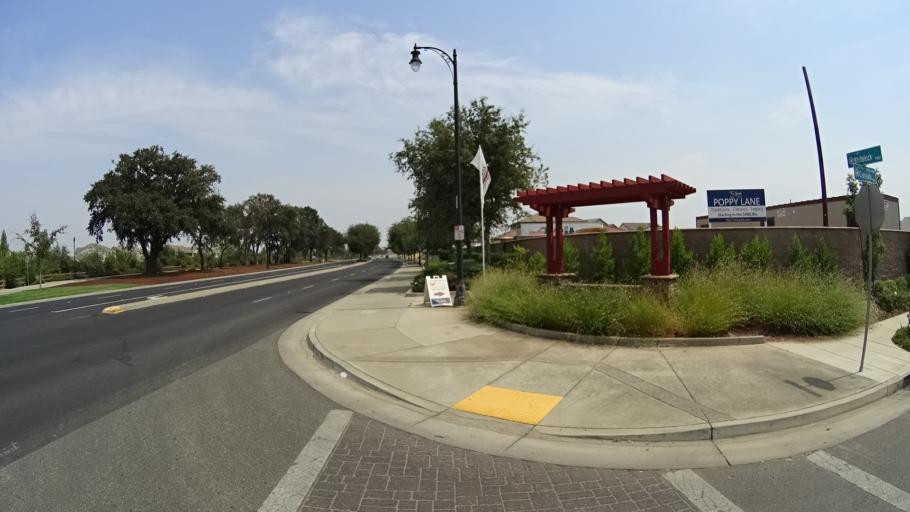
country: US
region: California
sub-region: Sacramento County
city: Laguna
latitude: 38.3941
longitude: -121.4031
